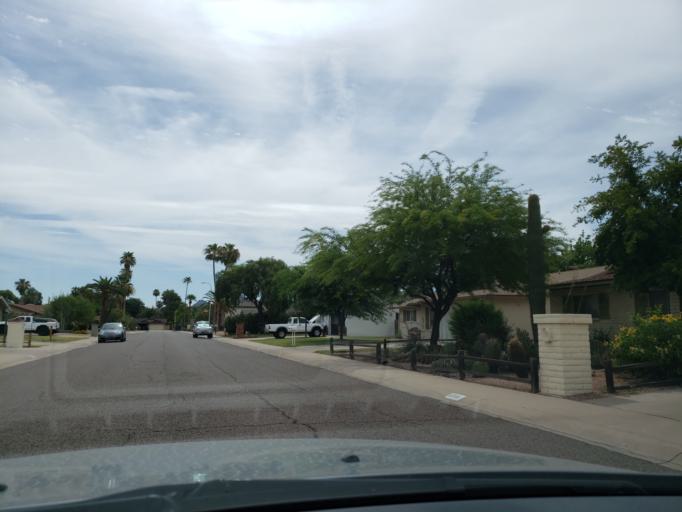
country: US
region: Arizona
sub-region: Maricopa County
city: Glendale
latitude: 33.5563
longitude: -112.0965
